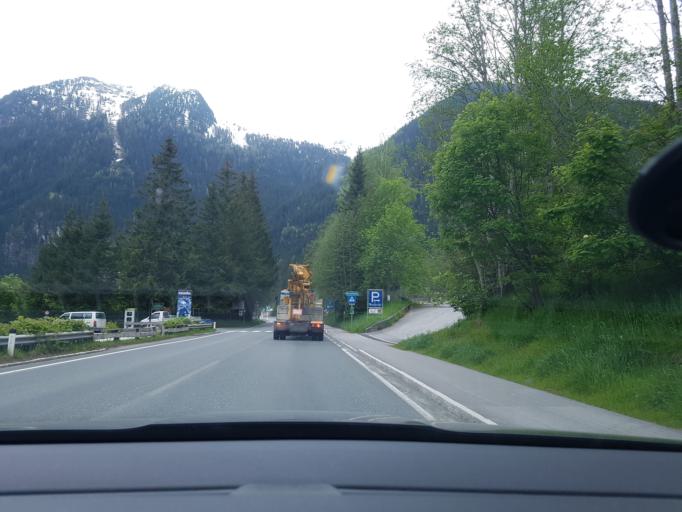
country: AT
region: Salzburg
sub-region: Politischer Bezirk Zell am See
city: Krimml
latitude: 47.2165
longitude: 12.1728
